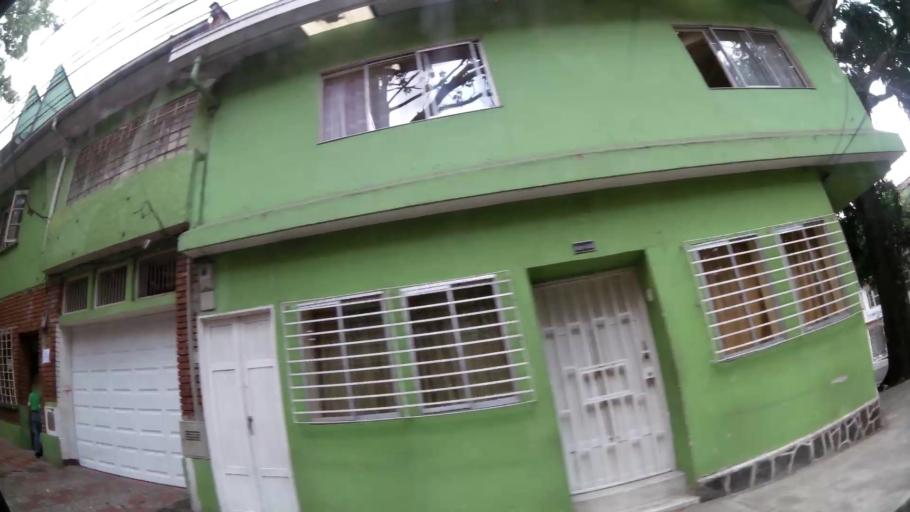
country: CO
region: Antioquia
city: Medellin
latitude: 6.2539
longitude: -75.5580
